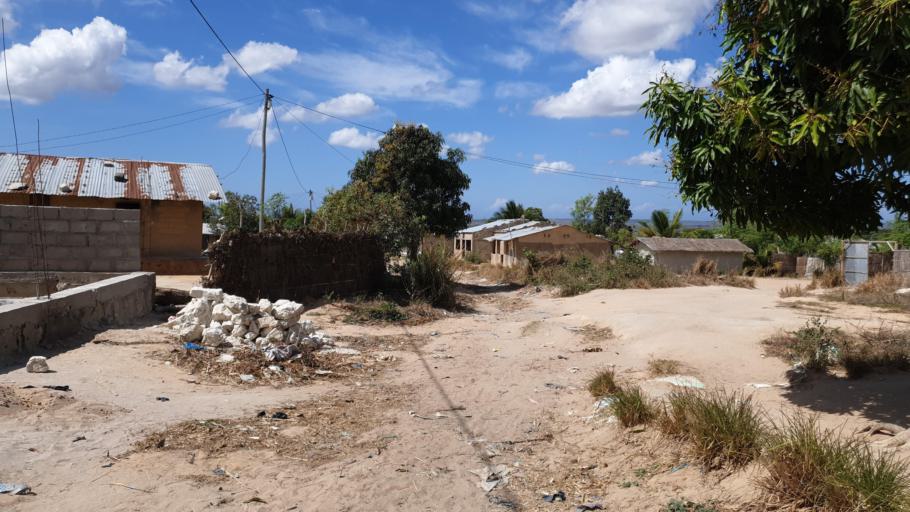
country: MZ
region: Nampula
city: Nacala
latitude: -14.5767
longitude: 40.7019
